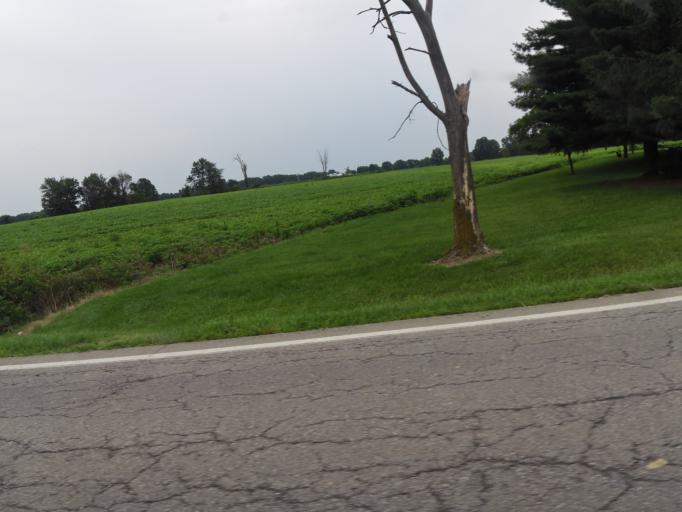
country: US
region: Ohio
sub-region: Clinton County
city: Blanchester
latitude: 39.2737
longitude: -83.9031
